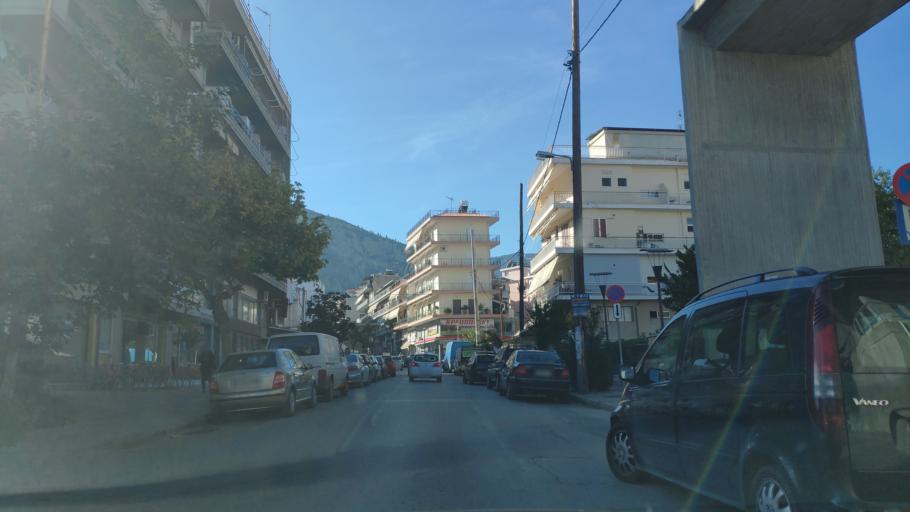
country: GR
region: Central Greece
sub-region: Nomos Voiotias
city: Livadeia
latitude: 38.4407
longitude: 22.8778
